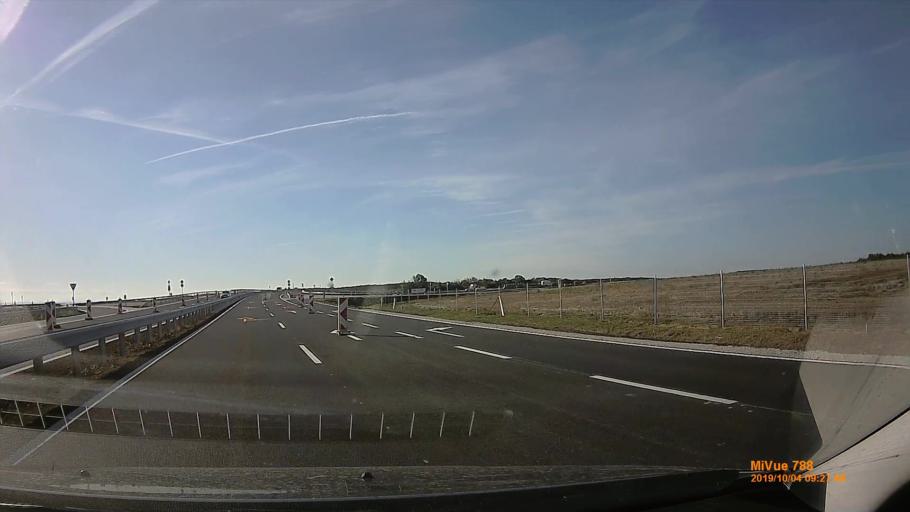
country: HU
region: Somogy
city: Kaposvar
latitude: 46.5028
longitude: 17.8098
